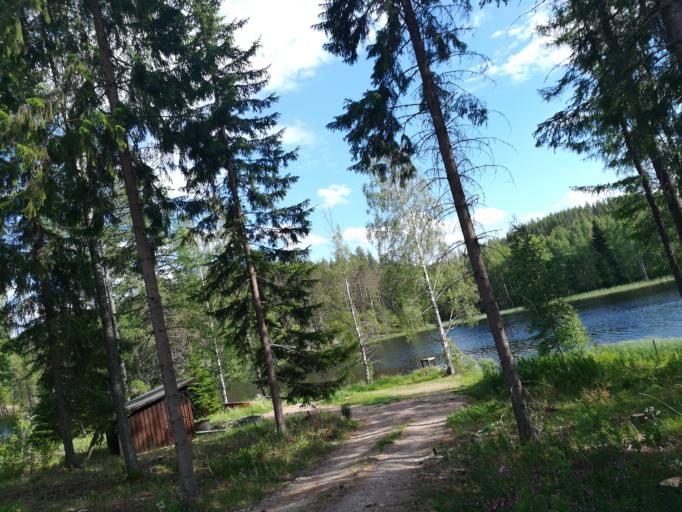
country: FI
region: South Karelia
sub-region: Imatra
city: Ruokolahti
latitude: 61.5443
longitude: 28.6891
